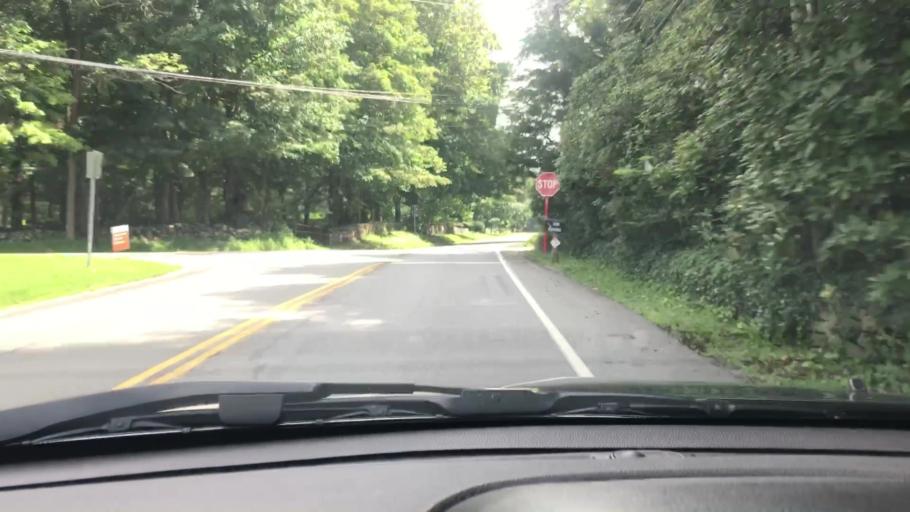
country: US
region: New York
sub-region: Westchester County
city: Bedford
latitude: 41.2194
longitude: -73.6579
